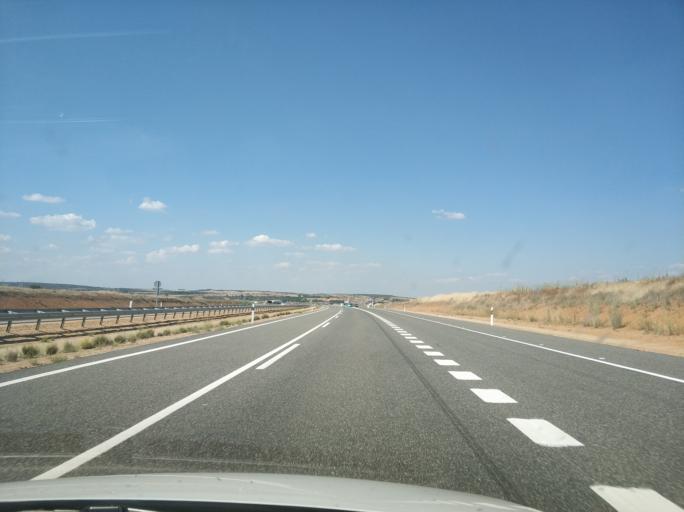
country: ES
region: Castille and Leon
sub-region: Provincia de Zamora
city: Granja de Moreruela
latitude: 41.7939
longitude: -5.7577
